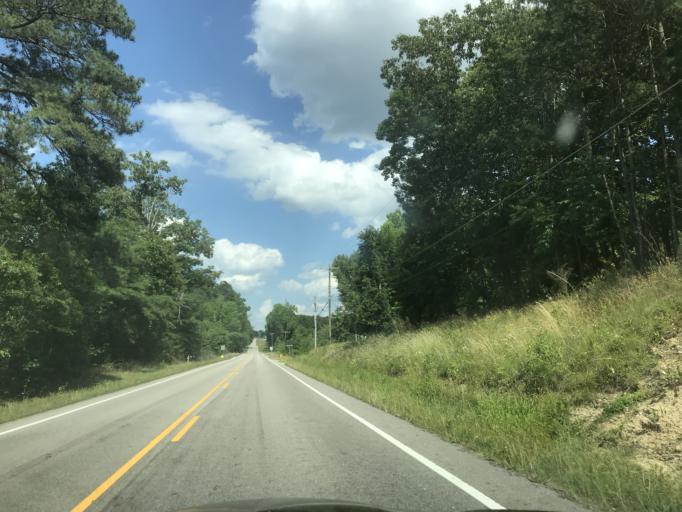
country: US
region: North Carolina
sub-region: Wake County
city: Zebulon
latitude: 35.9587
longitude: -78.2724
